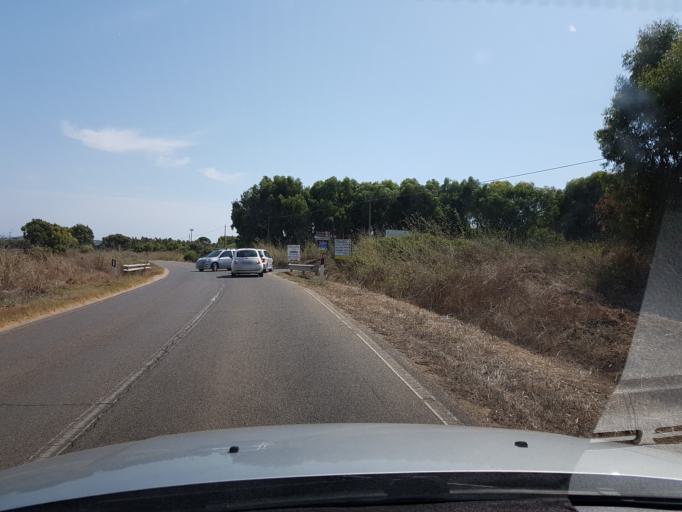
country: IT
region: Sardinia
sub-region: Provincia di Oristano
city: Cabras
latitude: 39.8985
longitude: 8.4346
